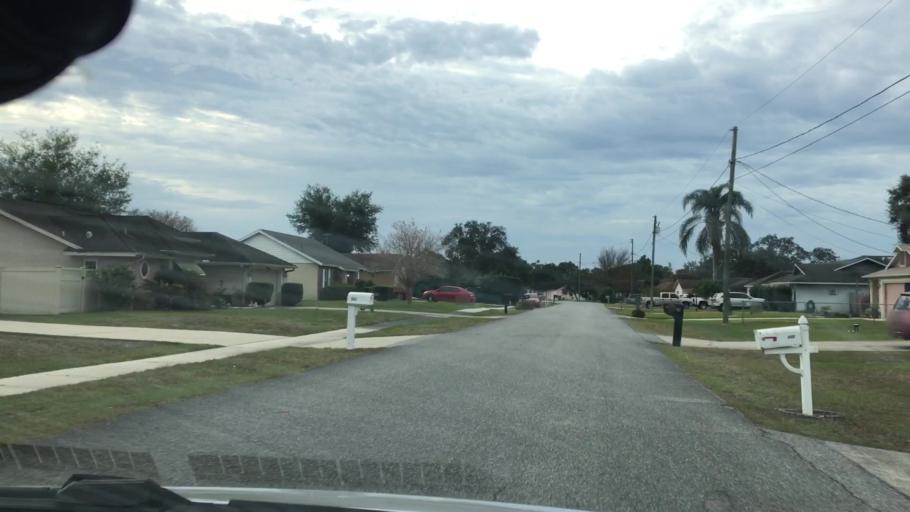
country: US
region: Florida
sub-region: Volusia County
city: Deltona
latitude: 28.8746
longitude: -81.2417
